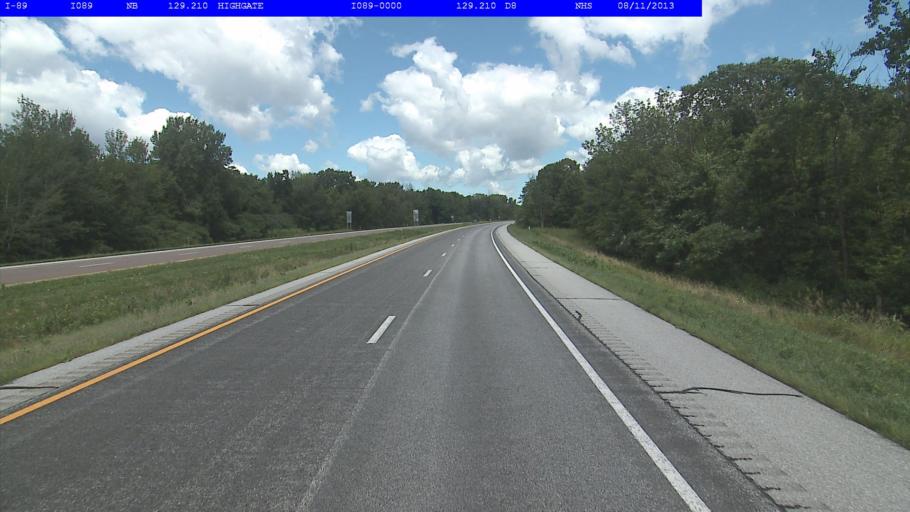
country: US
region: Vermont
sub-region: Franklin County
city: Swanton
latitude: 45.0005
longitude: -73.0867
